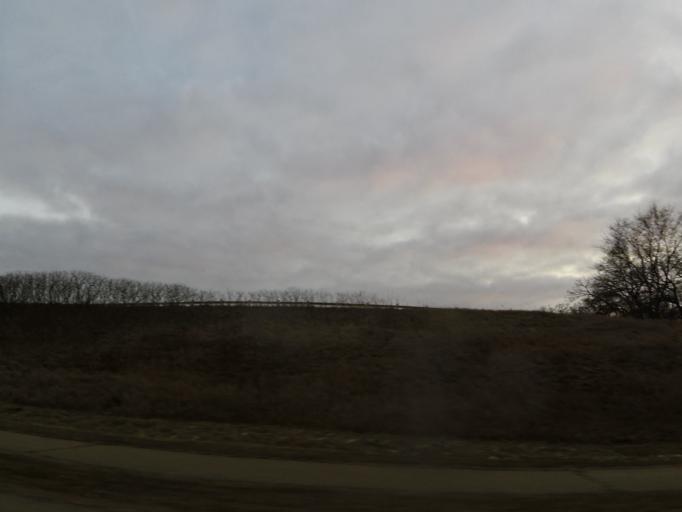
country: US
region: Minnesota
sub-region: Washington County
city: Grant
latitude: 45.0576
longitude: -92.8857
